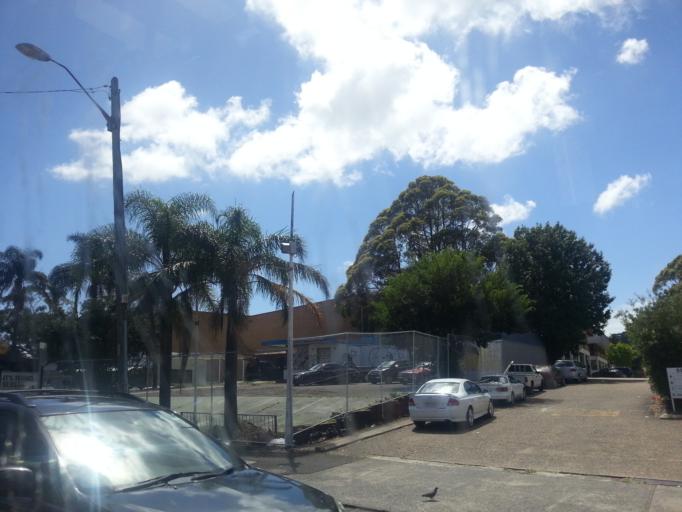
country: AU
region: New South Wales
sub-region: City of Sydney
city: Alexandria
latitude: -33.9090
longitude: 151.2027
